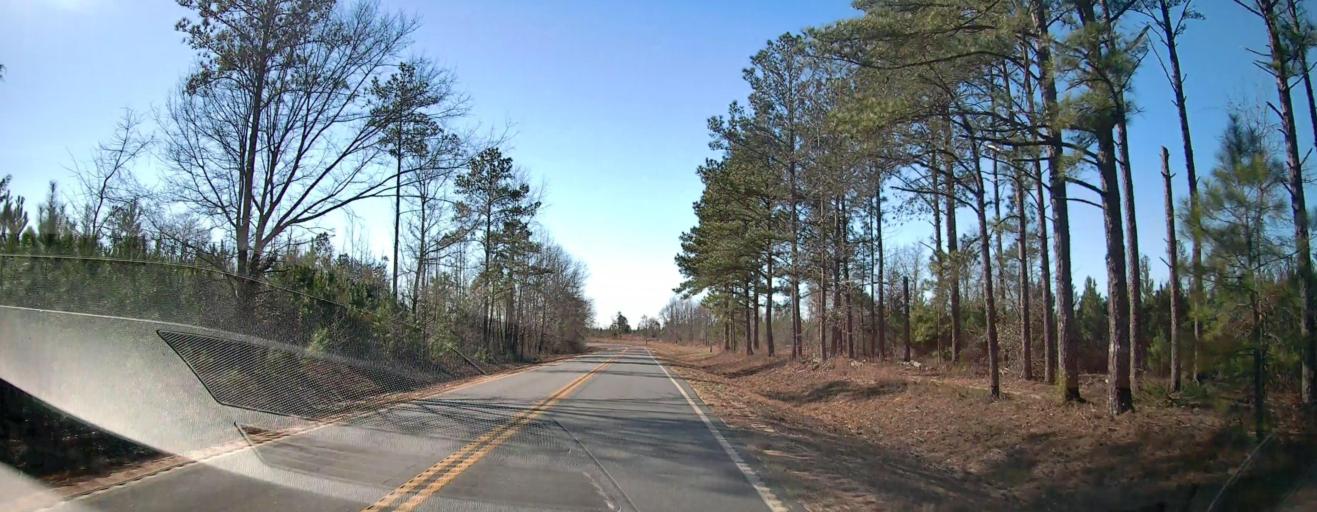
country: US
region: Georgia
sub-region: Taylor County
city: Butler
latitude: 32.6607
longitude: -84.3578
